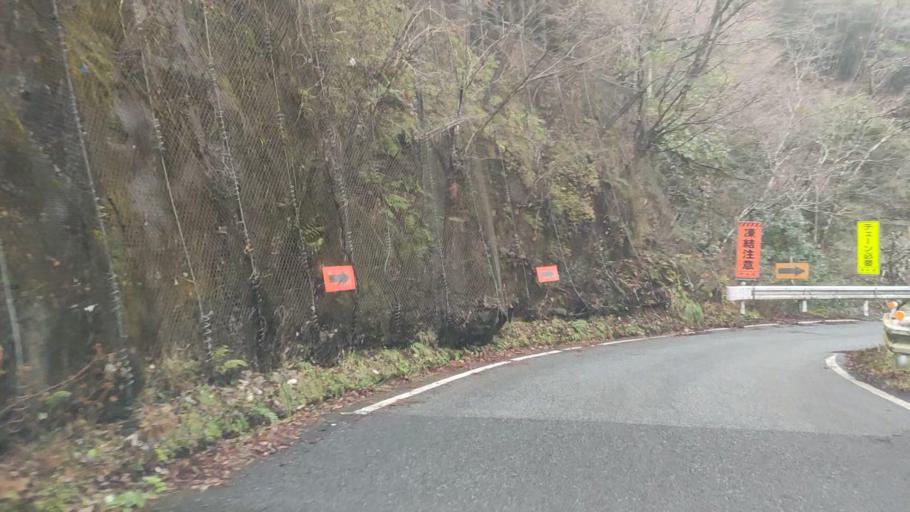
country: JP
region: Kumamoto
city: Matsubase
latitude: 32.4837
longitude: 130.8934
